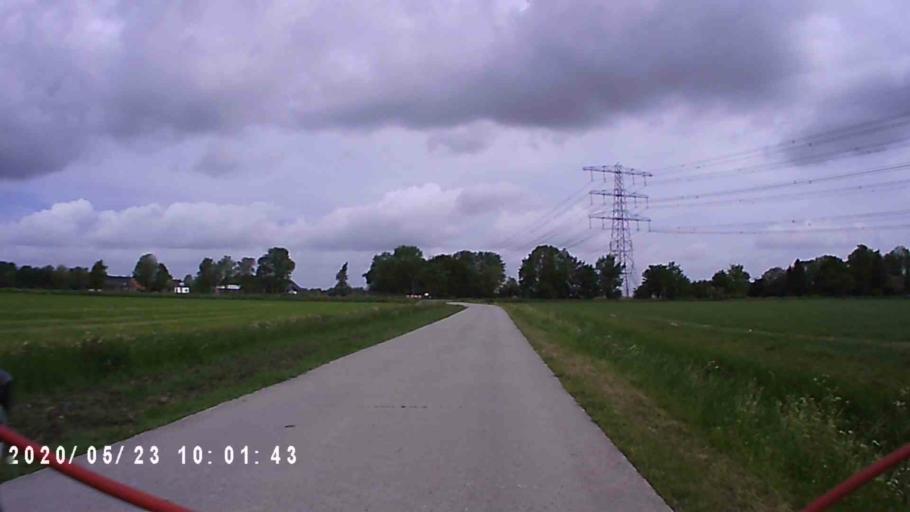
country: NL
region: Groningen
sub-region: Gemeente Appingedam
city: Appingedam
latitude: 53.3166
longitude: 6.8195
